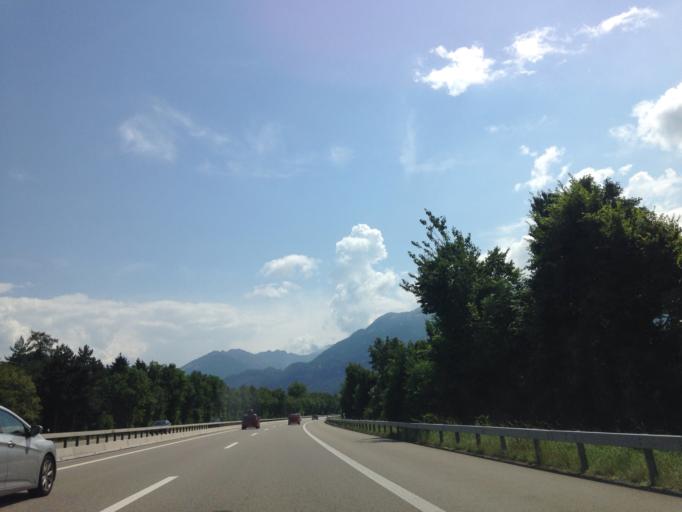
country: CH
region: Saint Gallen
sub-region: Wahlkreis Sarganserland
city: Sargans
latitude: 47.0546
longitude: 9.4705
